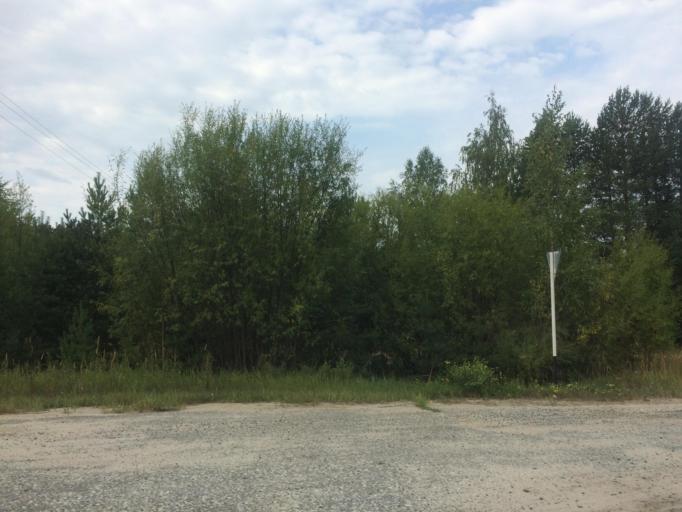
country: RU
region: Mariy-El
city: Yoshkar-Ola
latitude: 56.5429
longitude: 47.9815
